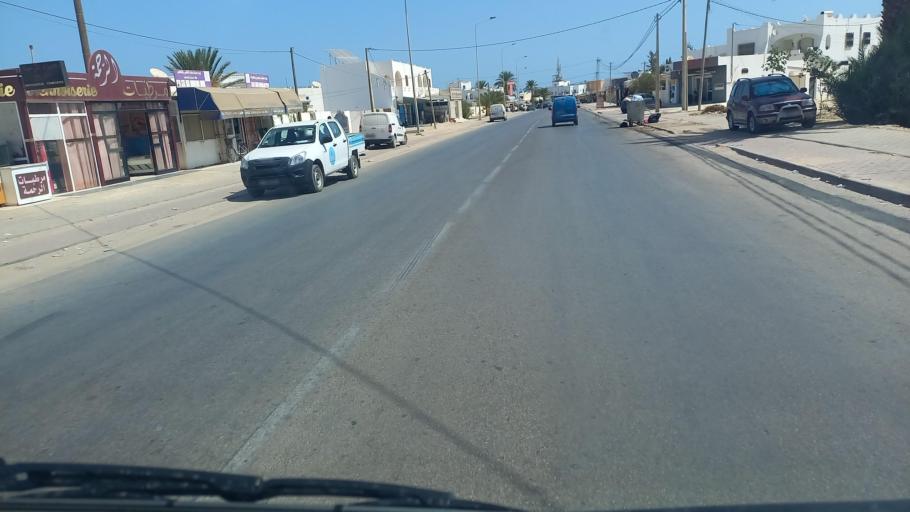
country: TN
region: Madanin
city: Houmt Souk
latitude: 33.8706
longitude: 10.8716
